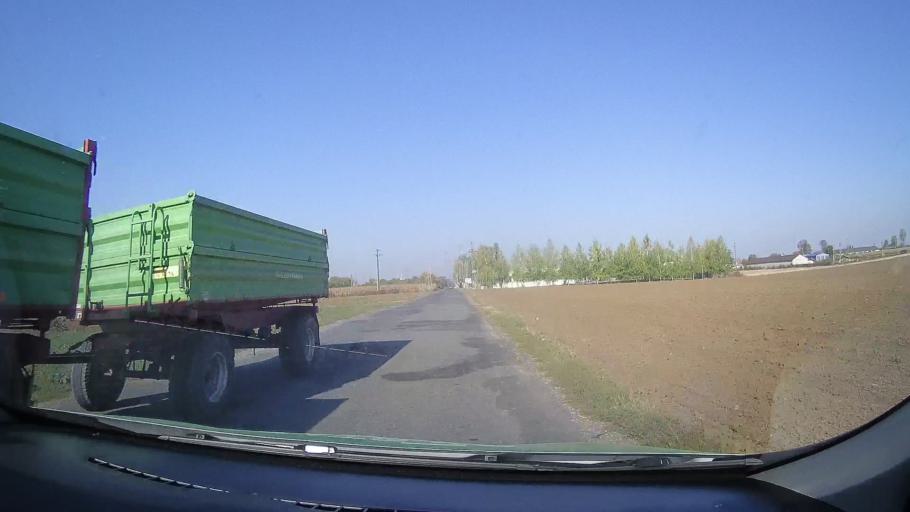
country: RO
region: Satu Mare
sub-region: Comuna Sanislau
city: Sanislau
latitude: 47.6274
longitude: 22.3372
